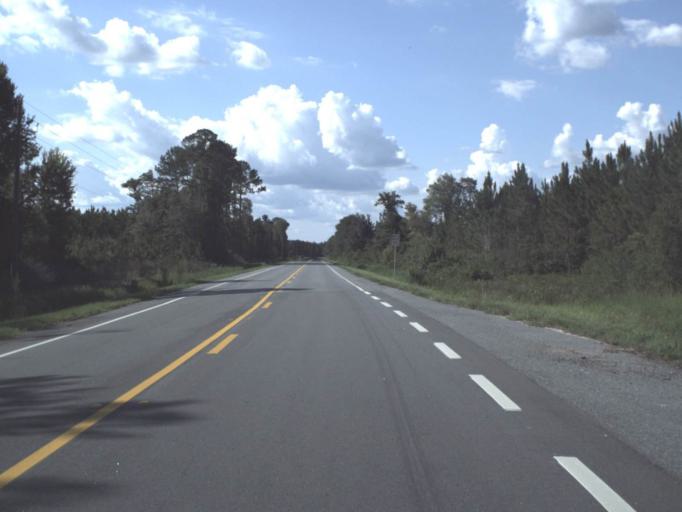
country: US
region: Florida
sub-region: Lafayette County
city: Mayo
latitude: 30.0096
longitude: -83.1926
